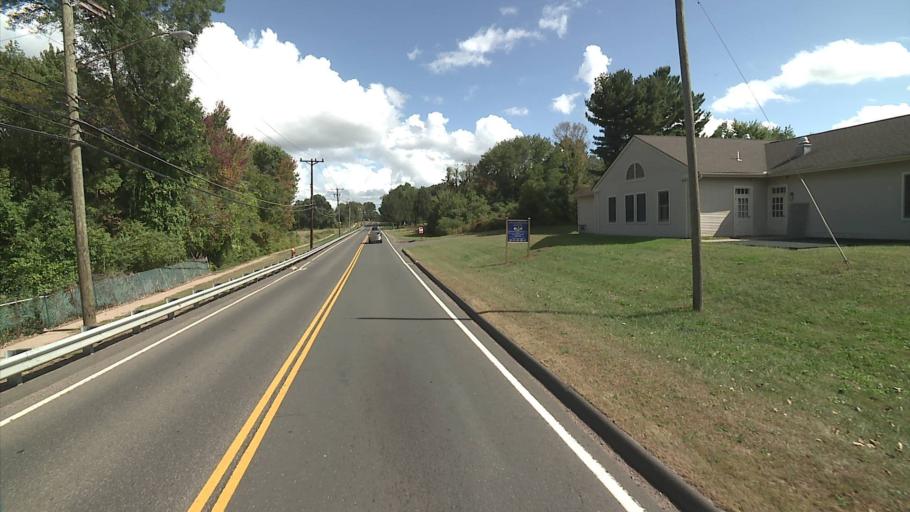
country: US
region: Connecticut
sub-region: Middlesex County
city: Cromwell
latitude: 41.6536
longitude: -72.6486
